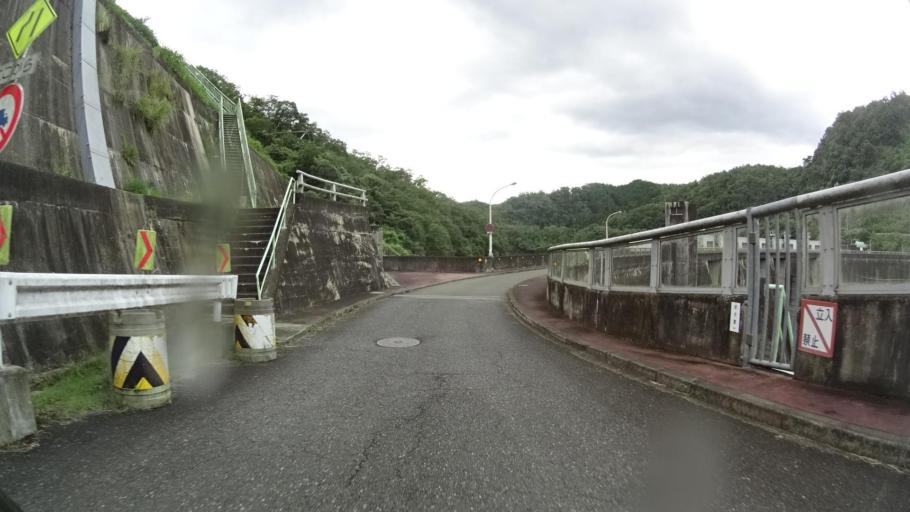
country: JP
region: Mie
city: Ueno-ebisumachi
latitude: 34.7579
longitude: 136.0093
